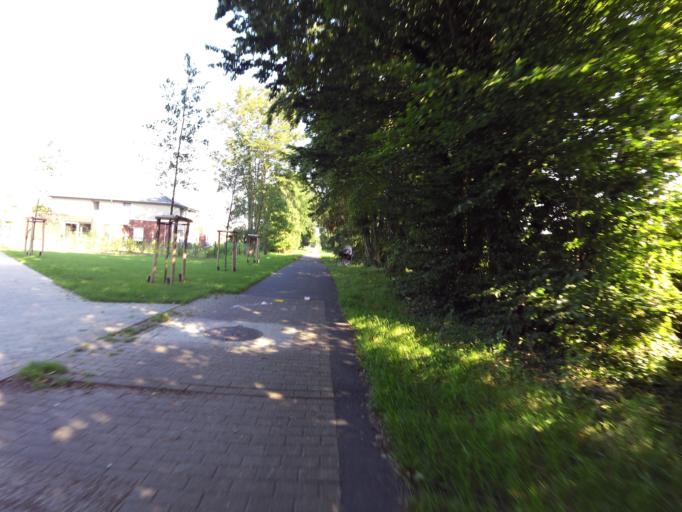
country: BE
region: Flanders
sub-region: Provincie West-Vlaanderen
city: Gistel
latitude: 51.1525
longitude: 2.9632
